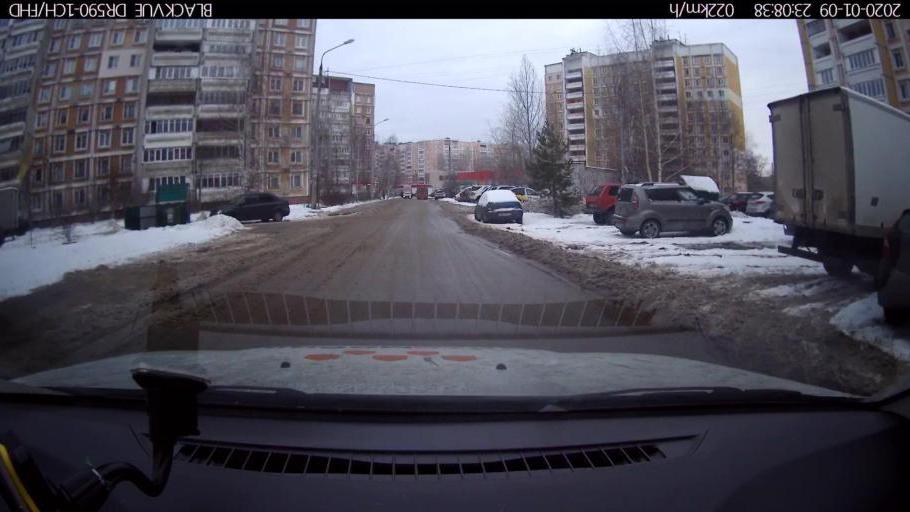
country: RU
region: Nizjnij Novgorod
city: Gorbatovka
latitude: 56.3678
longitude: 43.8003
